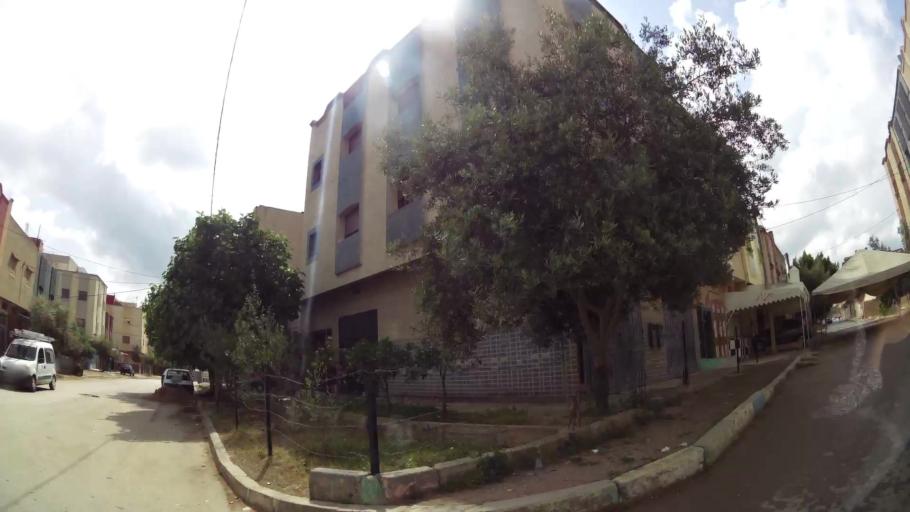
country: MA
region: Rabat-Sale-Zemmour-Zaer
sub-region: Khemisset
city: Tiflet
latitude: 33.8985
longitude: -6.3254
